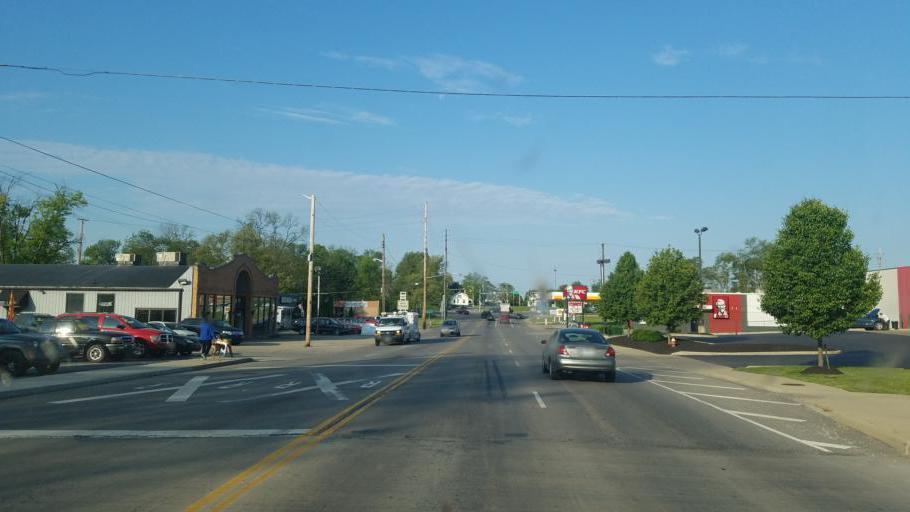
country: US
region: Ohio
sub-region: Fayette County
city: Washington Court House
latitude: 39.5339
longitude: -83.4426
